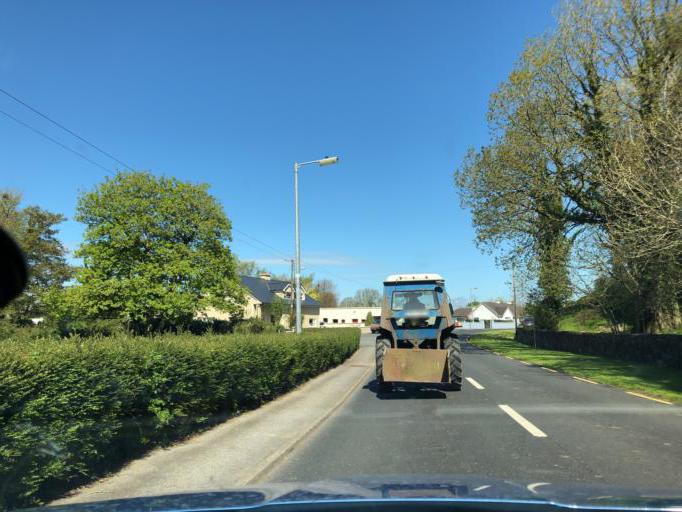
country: IE
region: Connaught
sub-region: County Galway
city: Portumna
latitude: 53.1466
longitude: -8.3715
